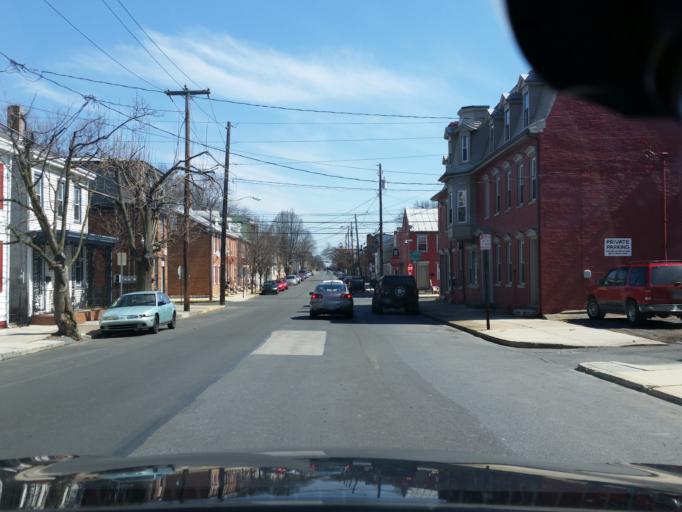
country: US
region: Pennsylvania
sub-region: Cumberland County
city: Carlisle
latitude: 40.2050
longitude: -77.1941
